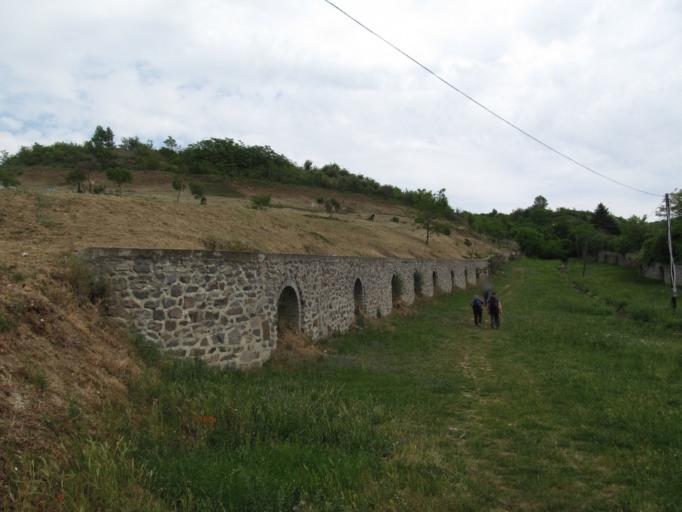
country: HU
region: Borsod-Abauj-Zemplen
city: Tarcal
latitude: 48.1247
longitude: 21.3517
